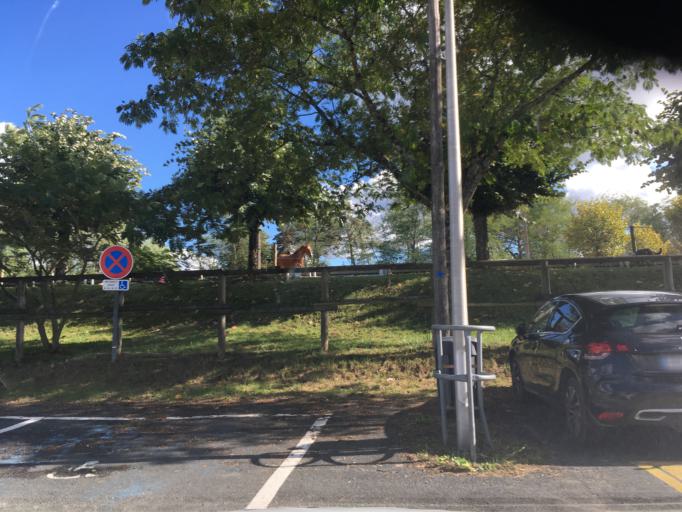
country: FR
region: Limousin
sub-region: Departement de la Correze
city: Brive-la-Gaillarde
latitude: 45.1414
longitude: 1.4941
